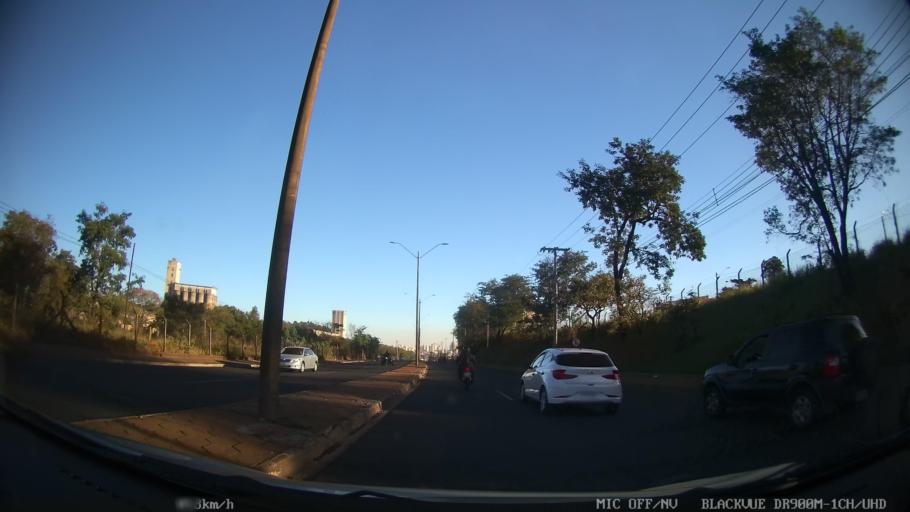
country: BR
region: Sao Paulo
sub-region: Araraquara
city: Araraquara
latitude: -21.7724
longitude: -48.1660
